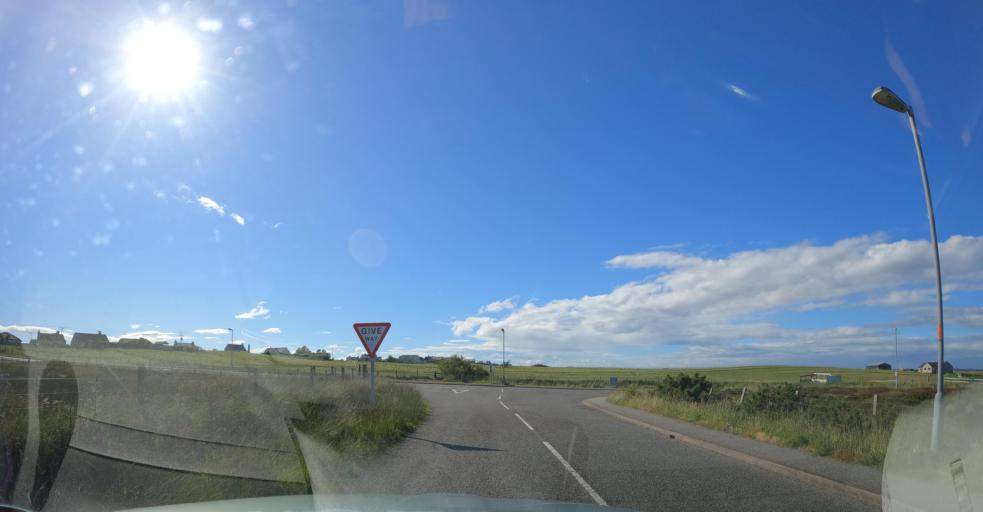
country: GB
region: Scotland
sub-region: Eilean Siar
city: Stornoway
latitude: 58.2160
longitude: -6.2371
